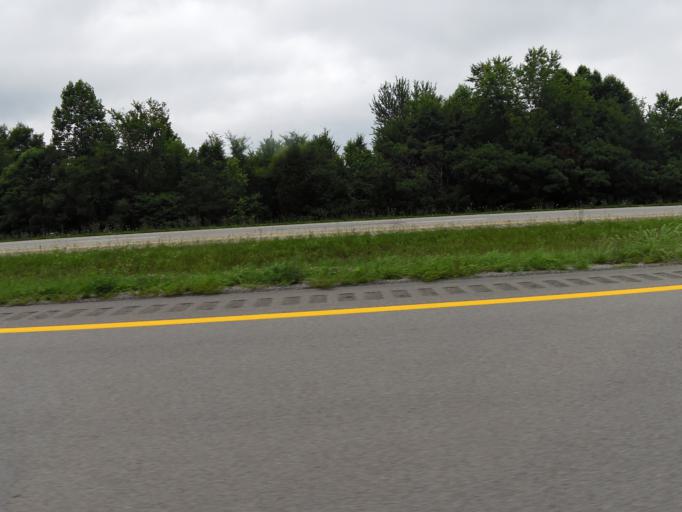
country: US
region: Kentucky
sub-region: Grayson County
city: Leitchfield
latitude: 37.4121
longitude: -86.5218
